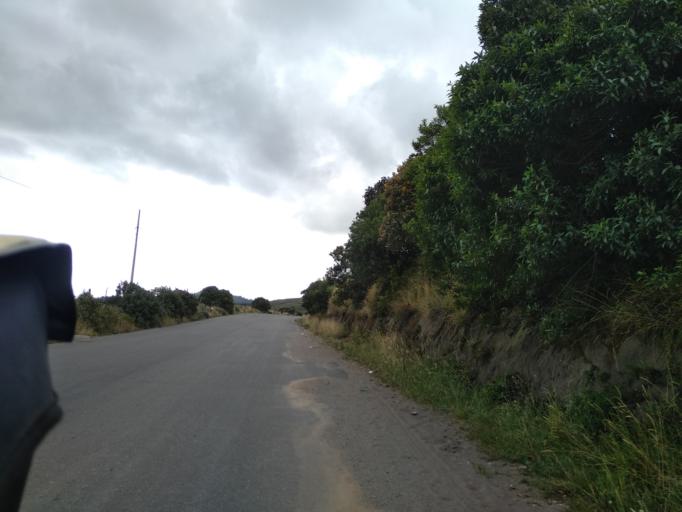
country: EC
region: Cotopaxi
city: Saquisili
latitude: -0.7222
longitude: -78.7616
